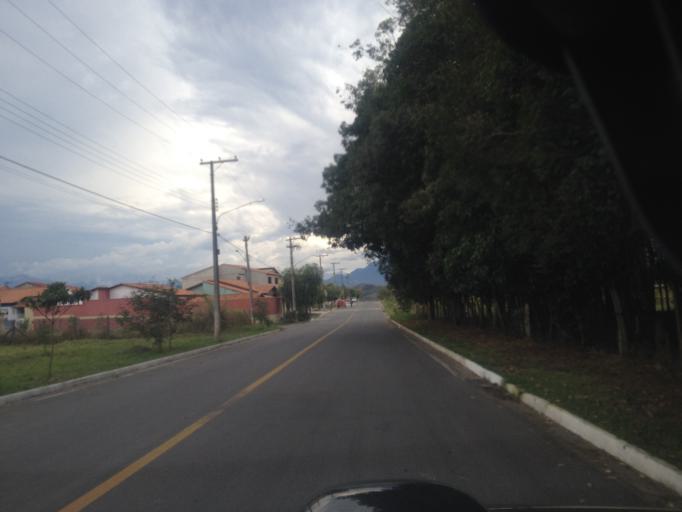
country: BR
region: Rio de Janeiro
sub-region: Porto Real
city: Porto Real
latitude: -22.4105
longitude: -44.3090
